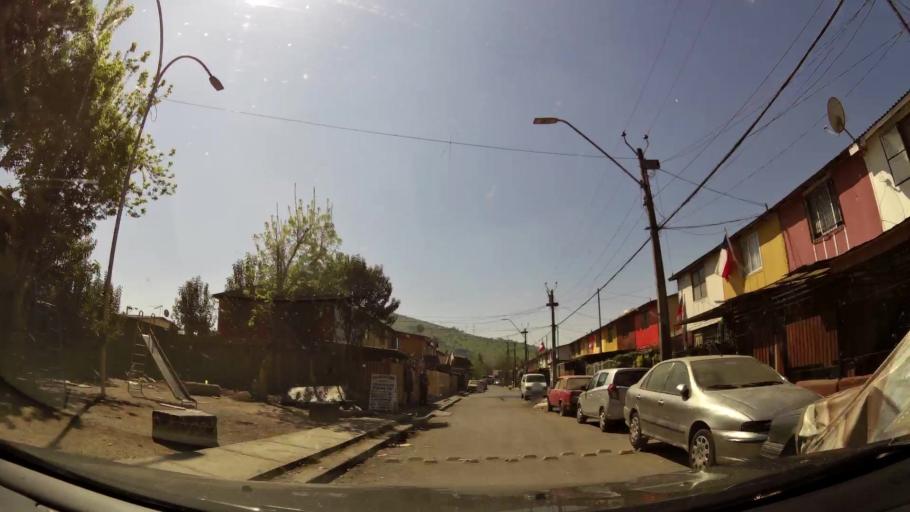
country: CL
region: Santiago Metropolitan
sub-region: Provincia de Santiago
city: Lo Prado
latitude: -33.4059
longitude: -70.7387
